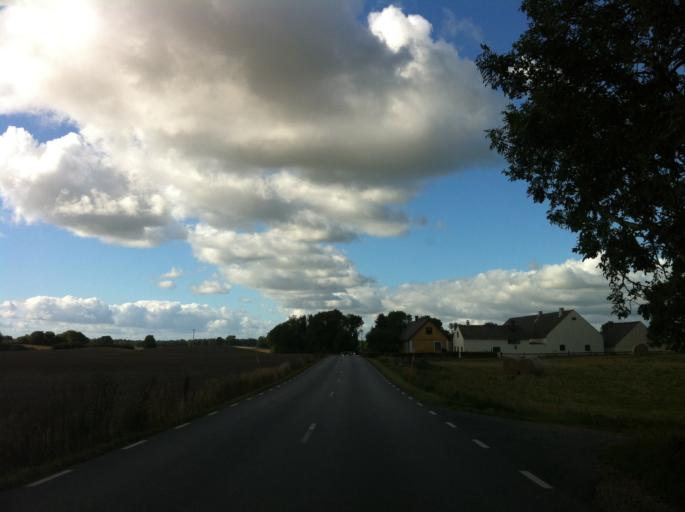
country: SE
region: Skane
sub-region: Tomelilla Kommun
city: Tomelilla
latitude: 55.6445
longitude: 13.9818
